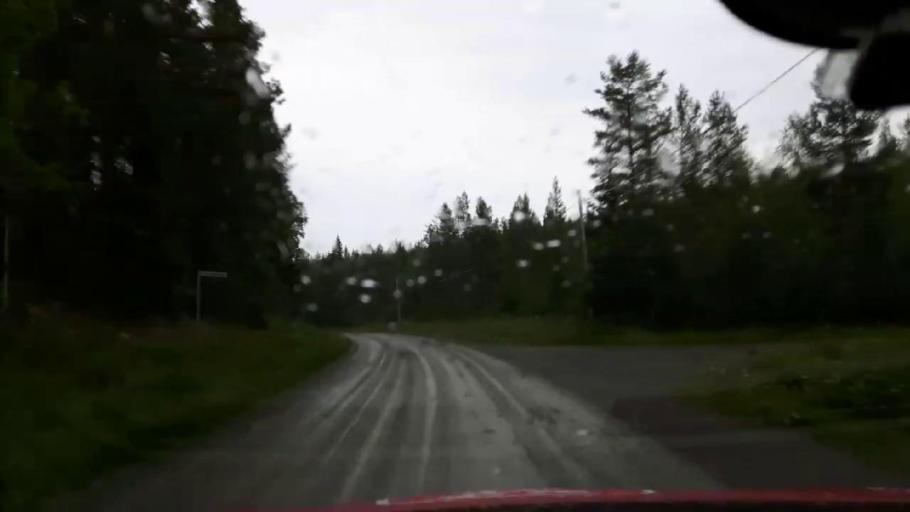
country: SE
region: Jaemtland
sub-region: OEstersunds Kommun
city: Brunflo
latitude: 62.8955
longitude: 14.8692
